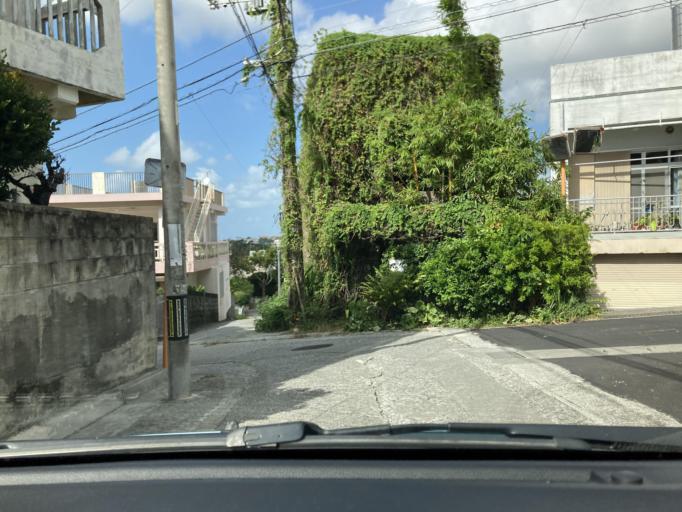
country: JP
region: Okinawa
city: Naha-shi
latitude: 26.2045
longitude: 127.7099
